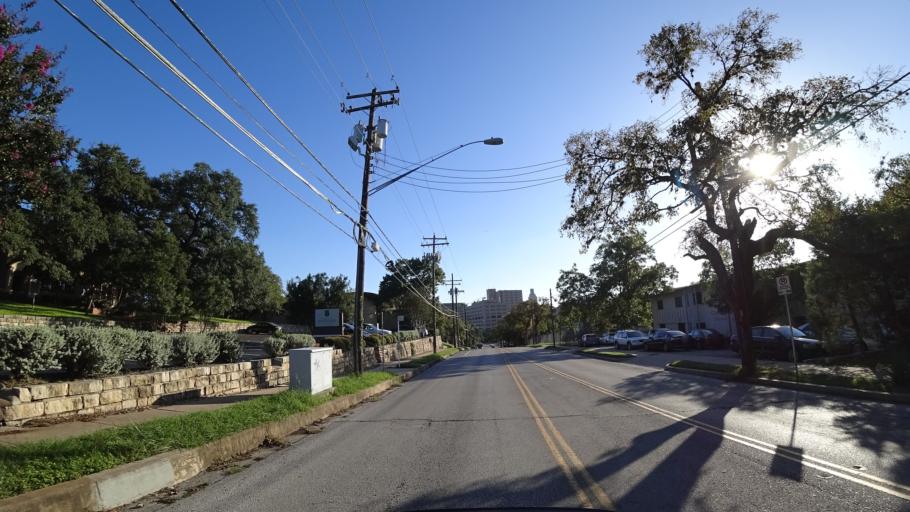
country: US
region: Texas
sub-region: Travis County
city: Austin
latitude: 30.2935
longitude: -97.7330
